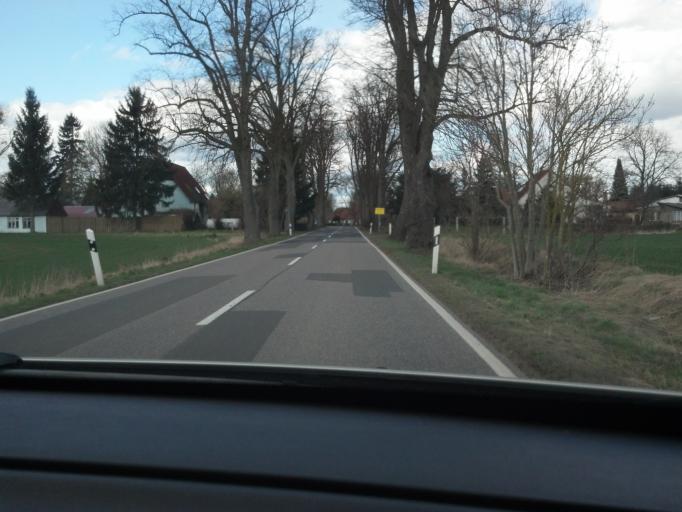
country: DE
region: Mecklenburg-Vorpommern
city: Loitz
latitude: 53.4192
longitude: 13.3574
